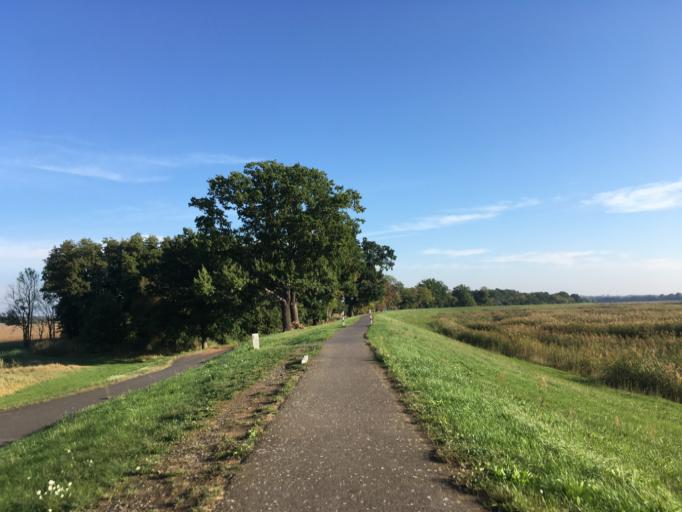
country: DE
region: Brandenburg
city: Reitwein
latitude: 52.4763
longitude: 14.6087
